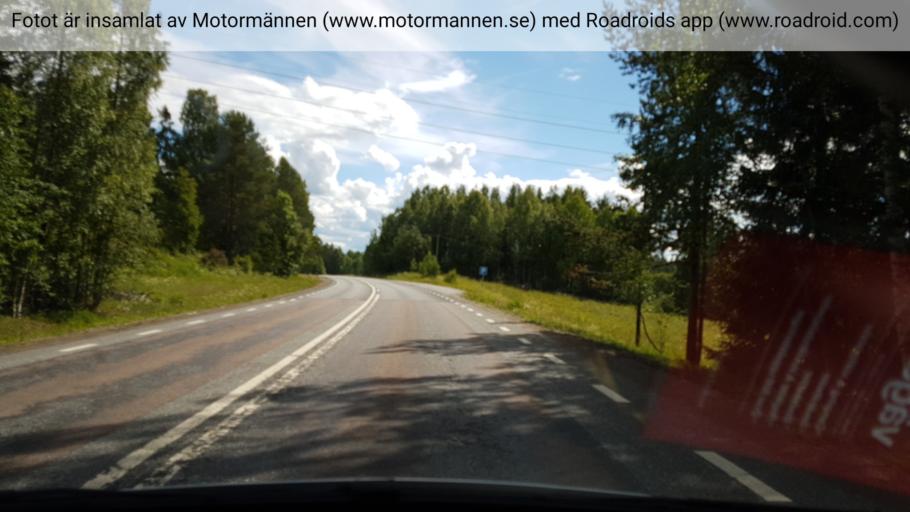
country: SE
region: Vaesternorrland
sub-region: Solleftea Kommun
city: Solleftea
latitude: 63.2703
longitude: 17.2084
